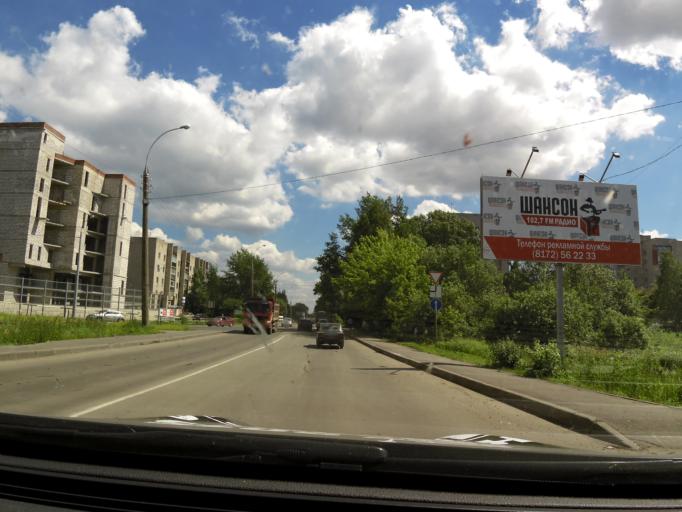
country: RU
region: Vologda
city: Vologda
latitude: 59.2271
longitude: 39.8607
